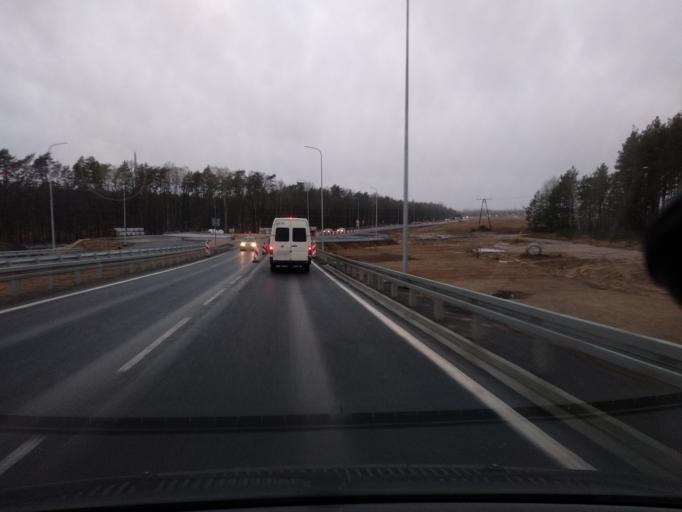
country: PL
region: Lower Silesian Voivodeship
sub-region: Powiat polkowicki
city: Polkowice
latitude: 51.4809
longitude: 16.0924
